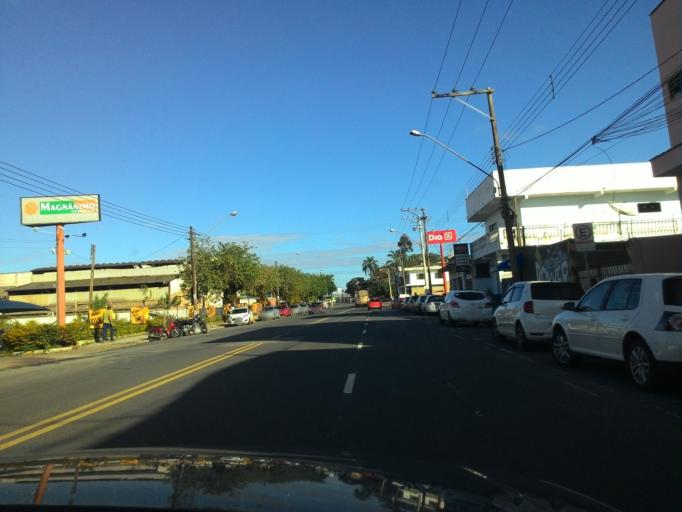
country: BR
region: Sao Paulo
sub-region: Registro
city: Registro
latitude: -24.4980
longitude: -47.8475
